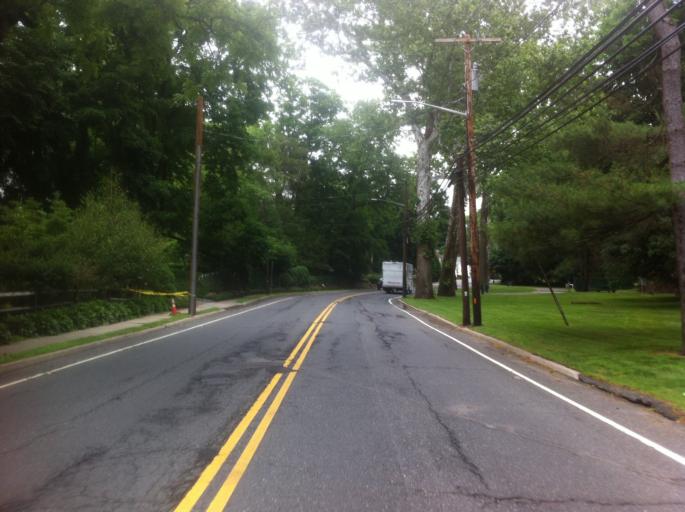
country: US
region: New York
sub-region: Nassau County
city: Locust Valley
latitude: 40.8784
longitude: -73.5889
